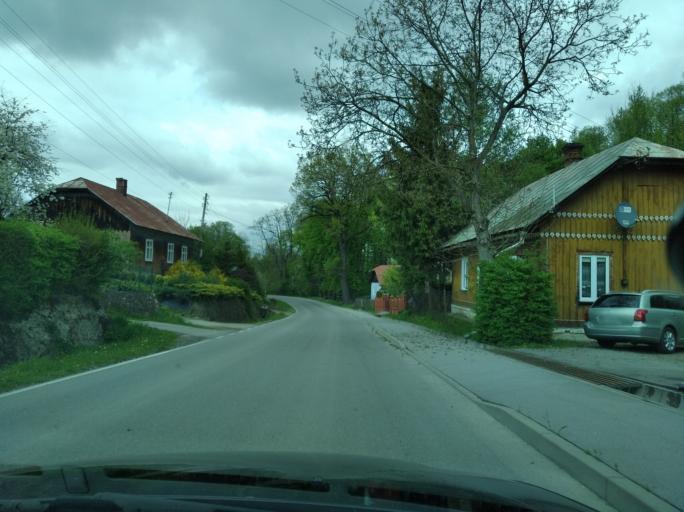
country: PL
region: Subcarpathian Voivodeship
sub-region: Powiat brzozowski
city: Turze Pole
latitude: 49.6409
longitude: 22.0001
